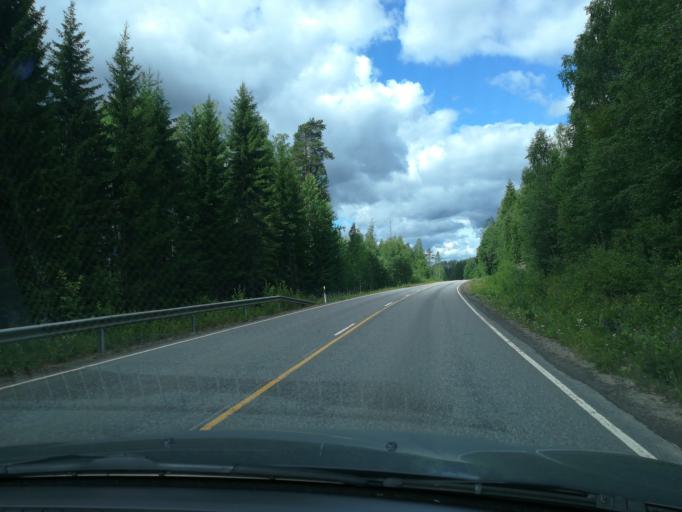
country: FI
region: Southern Savonia
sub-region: Mikkeli
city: Maentyharju
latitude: 61.3656
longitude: 26.9406
